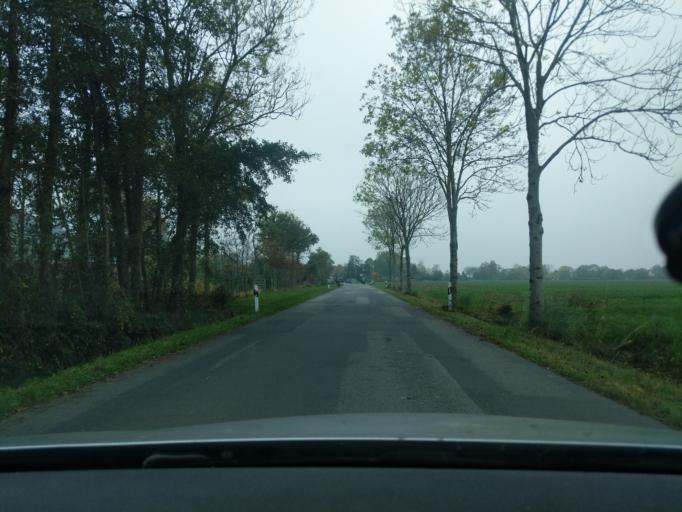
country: DE
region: Lower Saxony
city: Nordleda
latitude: 53.8276
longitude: 8.7840
